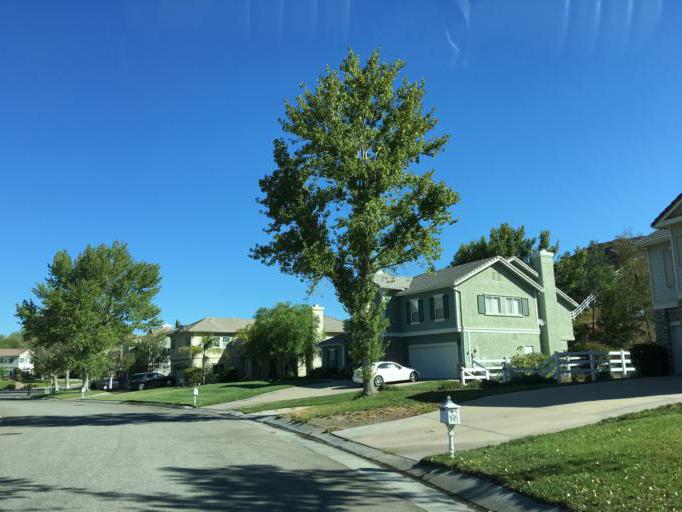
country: US
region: California
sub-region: Los Angeles County
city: Agua Dulce
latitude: 34.4004
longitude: -118.4017
